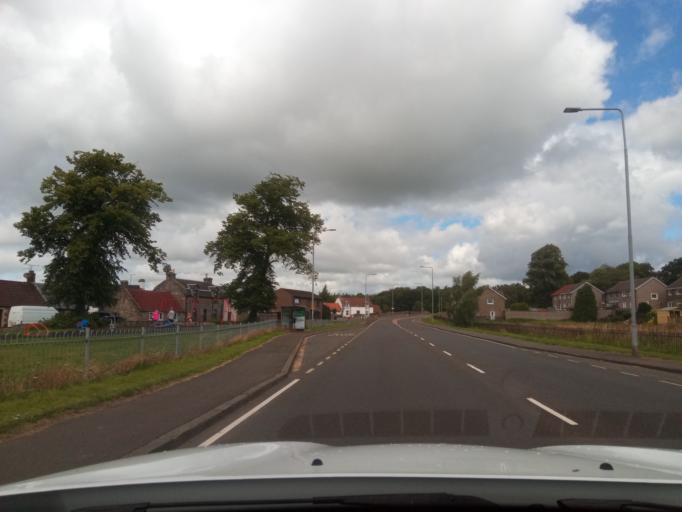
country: GB
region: Scotland
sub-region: Fife
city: Kincardine
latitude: 56.0731
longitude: -3.7203
